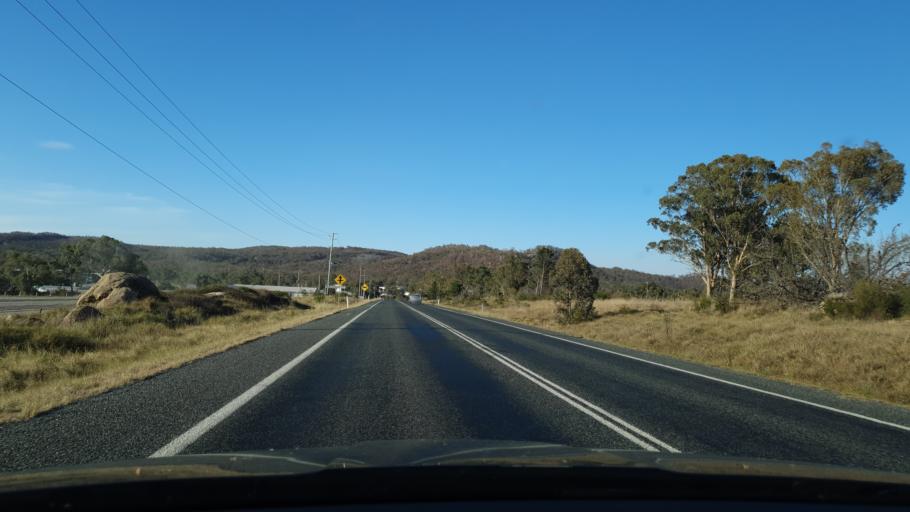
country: AU
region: Queensland
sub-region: Southern Downs
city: Stanthorpe
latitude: -28.6593
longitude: 151.9167
